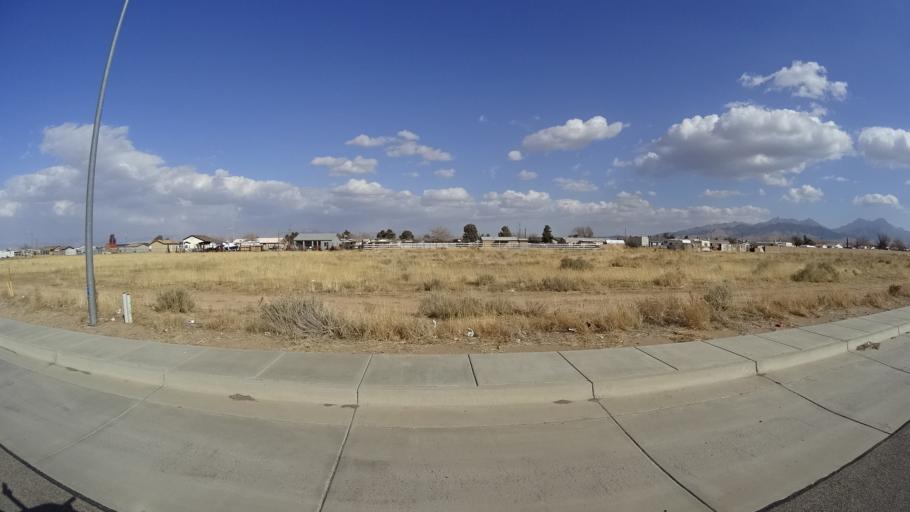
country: US
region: Arizona
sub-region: Mohave County
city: New Kingman-Butler
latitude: 35.2371
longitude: -114.0115
